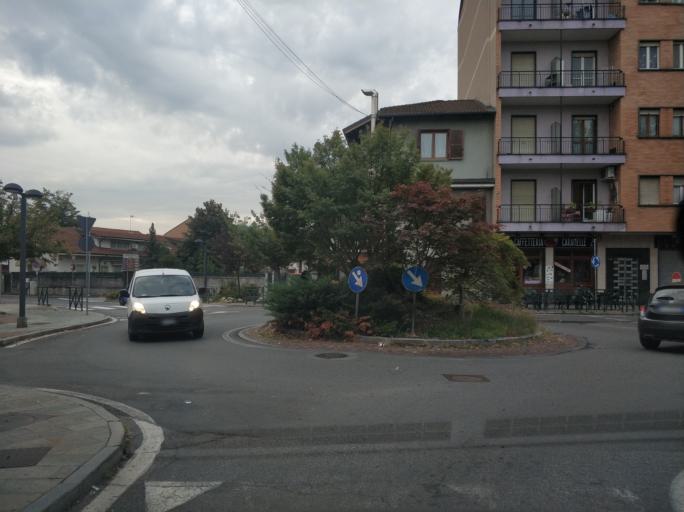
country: IT
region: Piedmont
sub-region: Provincia di Torino
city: Settimo Torinese
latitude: 45.1368
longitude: 7.7725
